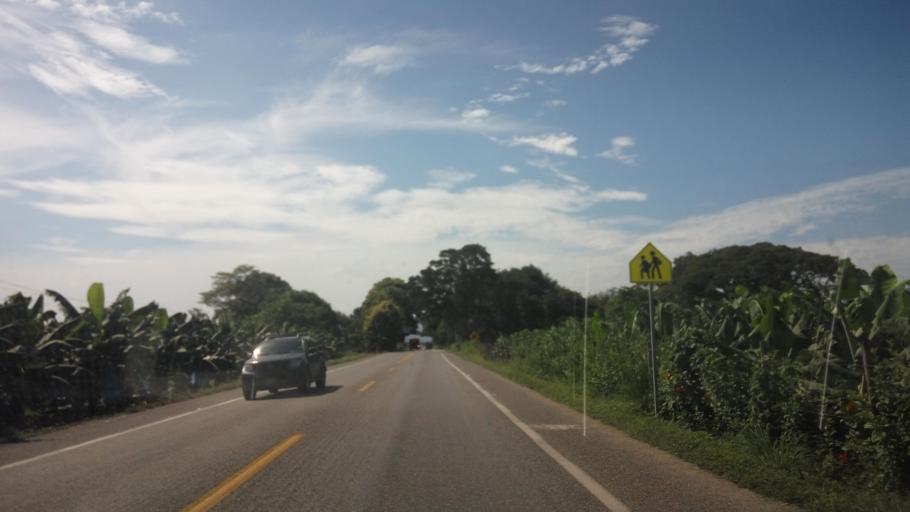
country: MX
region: Tabasco
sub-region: Teapa
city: Eureka y Belen
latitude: 17.6298
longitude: -92.9644
